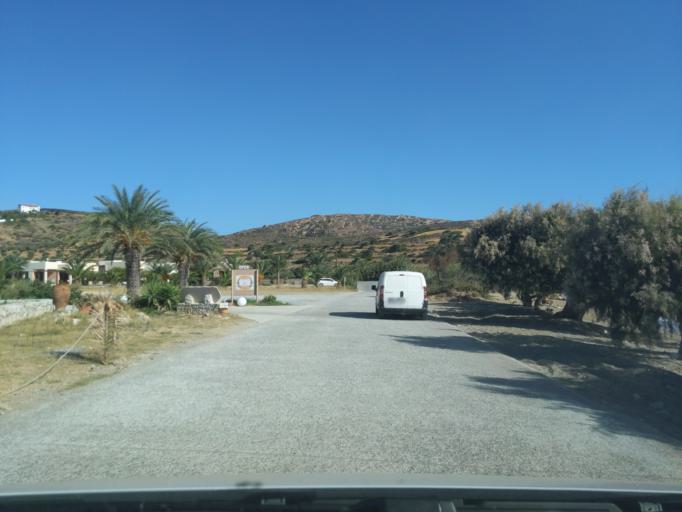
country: GR
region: Crete
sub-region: Nomos Lasithiou
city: Palekastro
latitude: 35.2142
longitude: 26.2675
